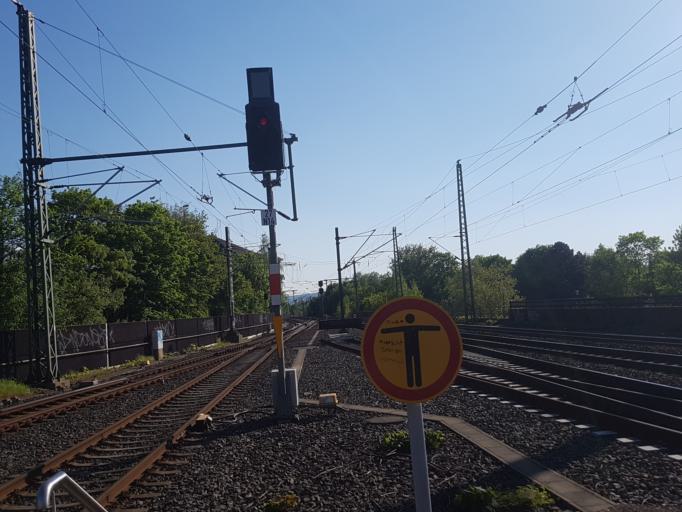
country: DE
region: North Rhine-Westphalia
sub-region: Regierungsbezirk Koln
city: Dueren
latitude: 50.8089
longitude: 6.4818
